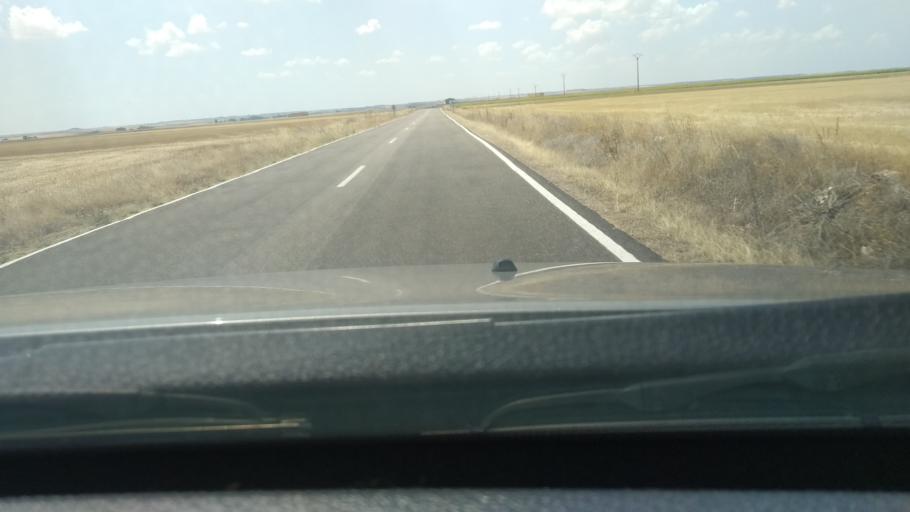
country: ES
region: Castille and Leon
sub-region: Provincia de Burgos
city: Villafruela
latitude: 41.9374
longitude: -3.8757
